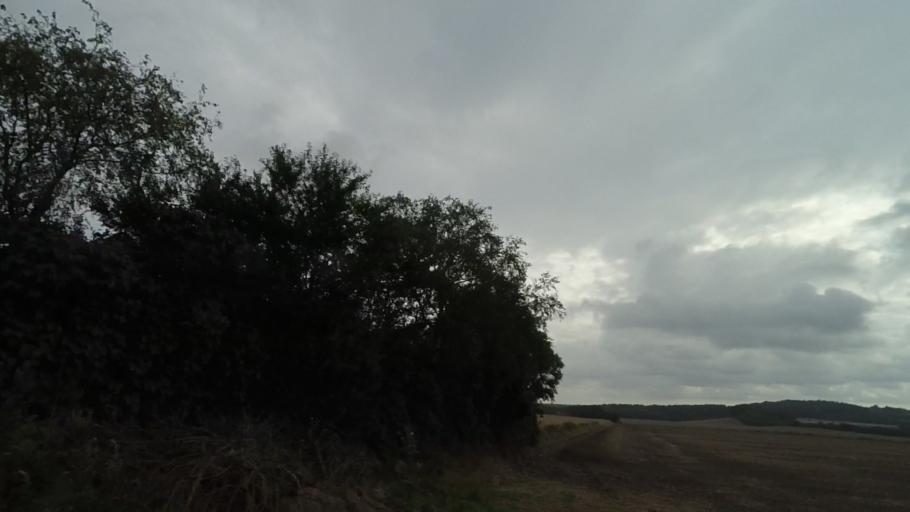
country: DK
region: Central Jutland
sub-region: Syddjurs Kommune
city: Ronde
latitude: 56.3305
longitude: 10.4581
